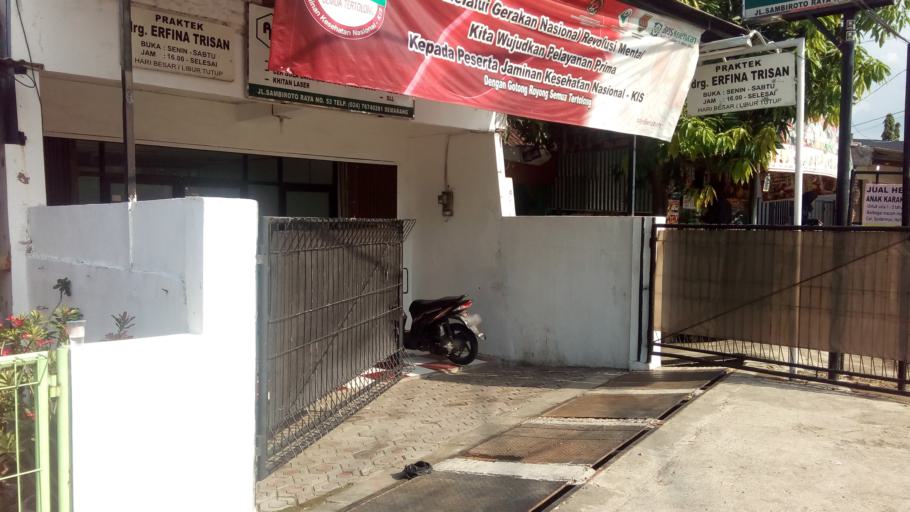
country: ID
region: Central Java
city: Semarang
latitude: -7.0254
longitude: 110.4600
